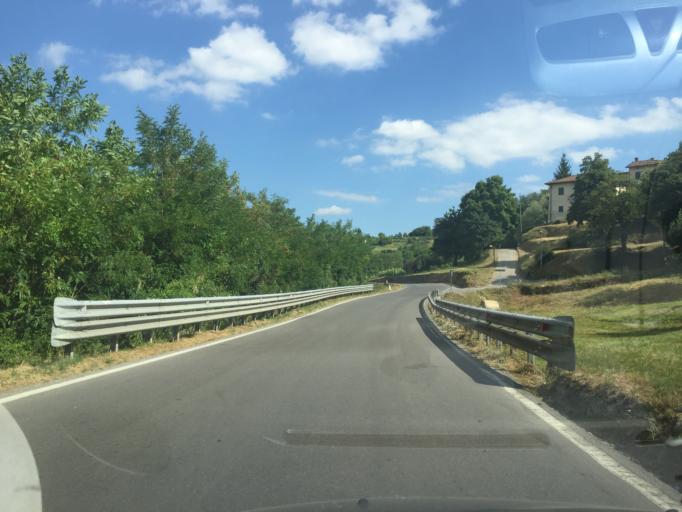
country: IT
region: Tuscany
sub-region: Provincia di Lucca
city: Pieve Fosciana
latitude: 44.1310
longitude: 10.3757
